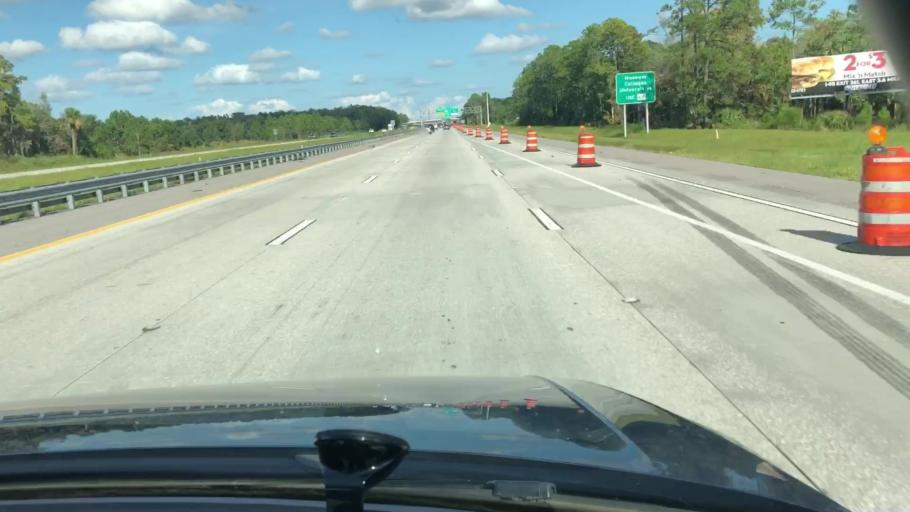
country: US
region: Florida
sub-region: Volusia County
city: South Daytona
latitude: 29.1473
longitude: -81.0945
